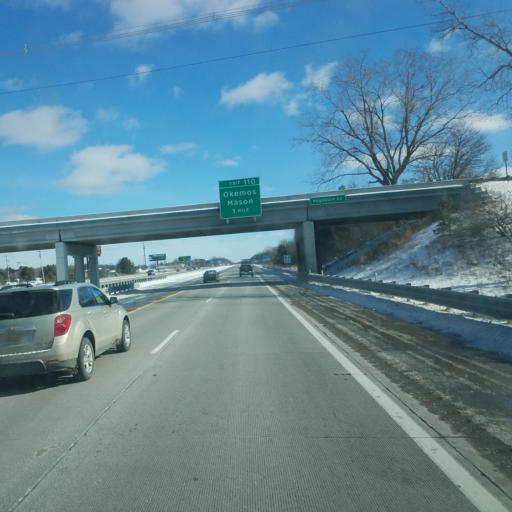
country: US
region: Michigan
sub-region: Ingham County
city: Okemos
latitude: 42.6778
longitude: -84.4630
